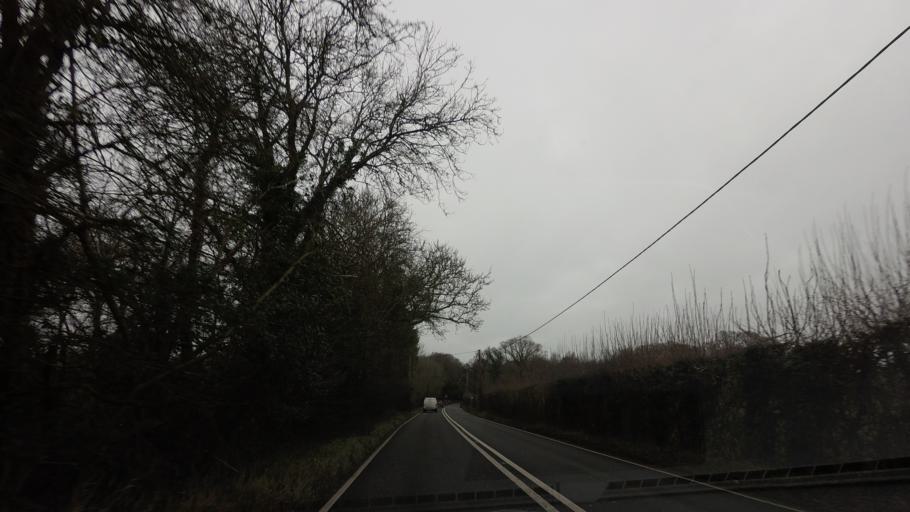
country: GB
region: England
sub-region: East Sussex
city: Battle
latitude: 50.9163
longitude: 0.5386
